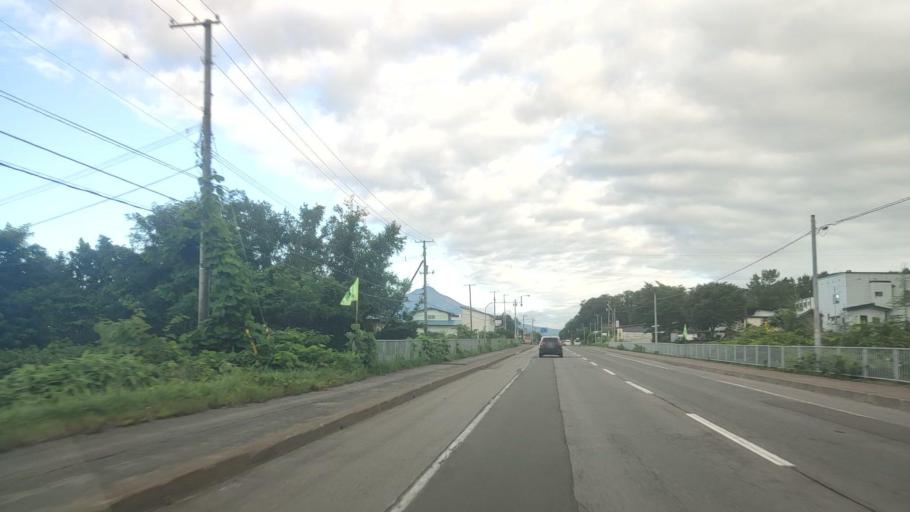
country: JP
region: Hokkaido
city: Nanae
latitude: 42.1158
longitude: 140.5409
